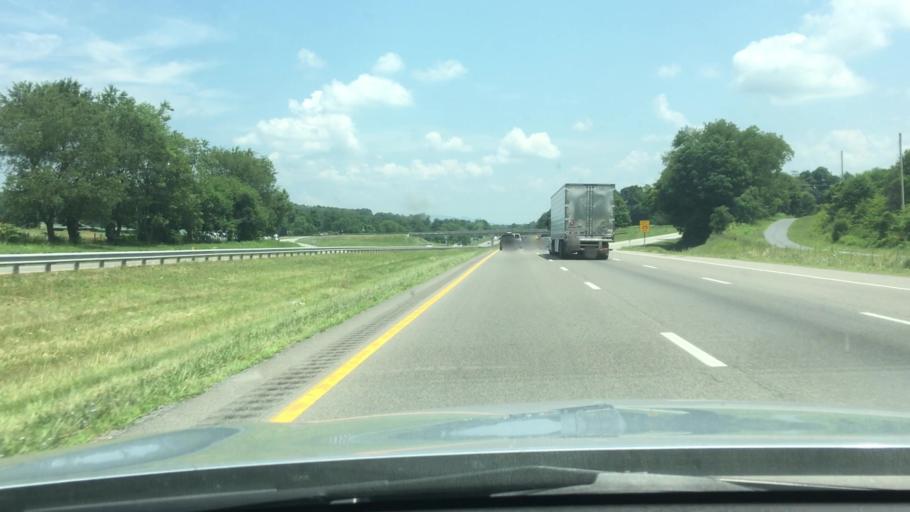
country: US
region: Virginia
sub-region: Washington County
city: Emory
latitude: 36.7649
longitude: -81.8372
